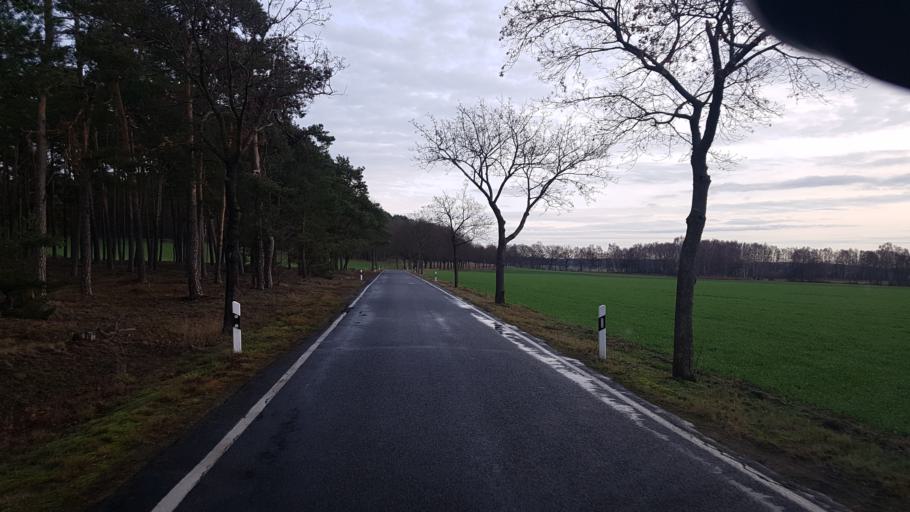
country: DE
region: Brandenburg
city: Hohenbucko
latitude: 51.7421
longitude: 13.4499
